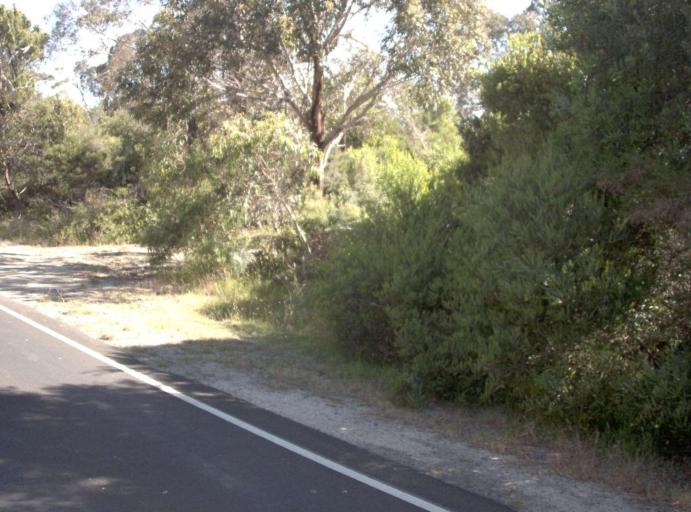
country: AU
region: Victoria
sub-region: Latrobe
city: Traralgon
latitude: -38.6481
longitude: 146.6737
